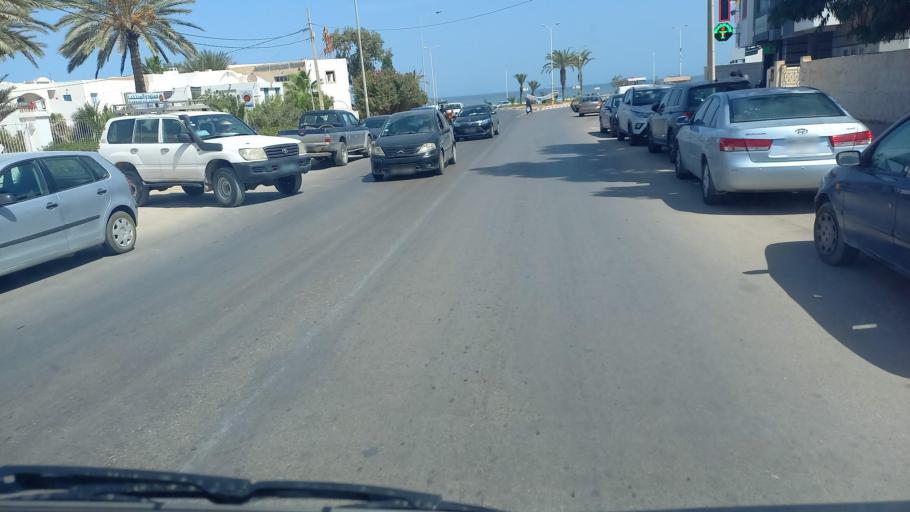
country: TN
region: Madanin
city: Houmt Souk
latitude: 33.8764
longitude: 10.8746
